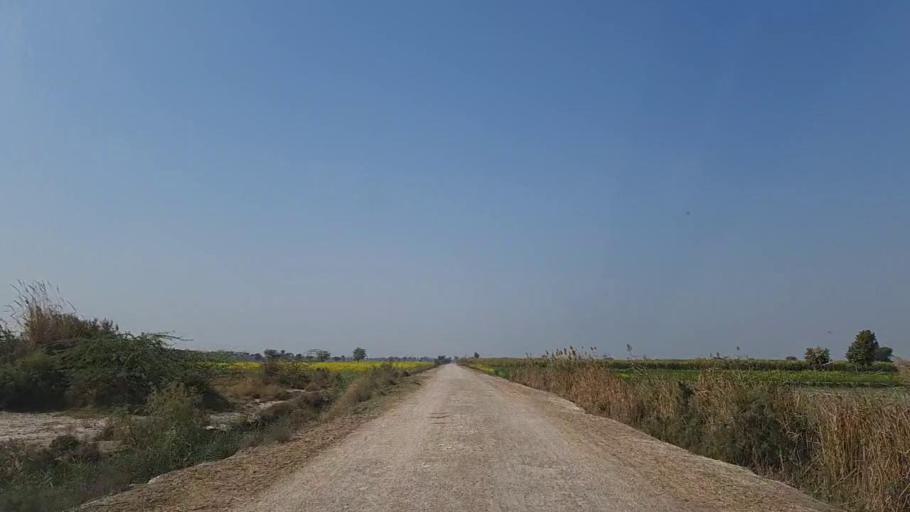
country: PK
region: Sindh
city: Daur
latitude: 26.4413
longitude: 68.2958
